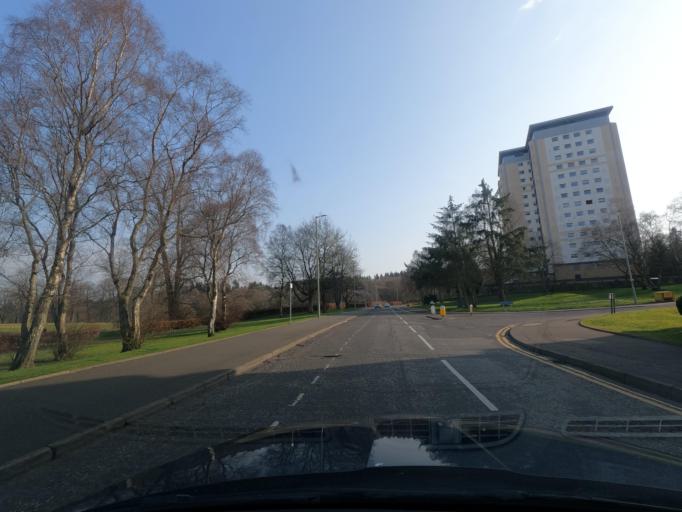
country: GB
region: Scotland
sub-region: Falkirk
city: Falkirk
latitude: 55.9956
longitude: -3.7785
